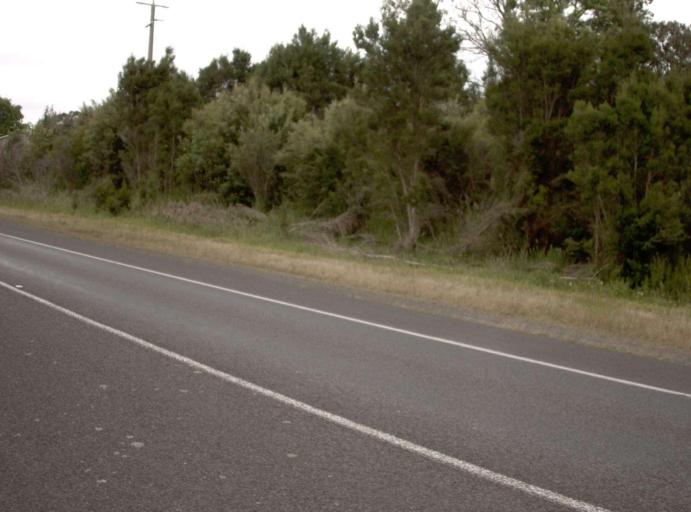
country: AU
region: Victoria
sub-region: Bass Coast
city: North Wonthaggi
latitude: -38.3660
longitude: 145.6965
